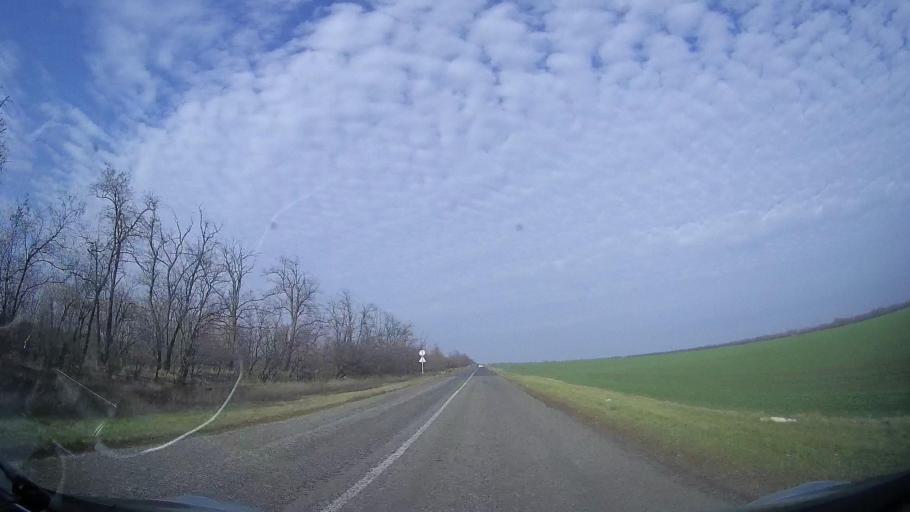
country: RU
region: Rostov
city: Gigant
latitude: 46.8466
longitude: 41.2868
